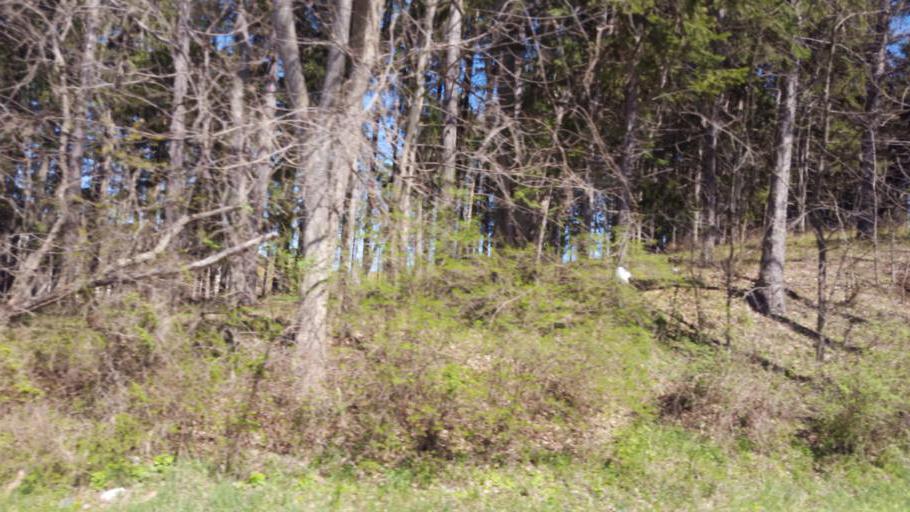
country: US
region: Ohio
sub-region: Belmont County
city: Saint Clairsville
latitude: 40.0777
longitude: -80.9156
